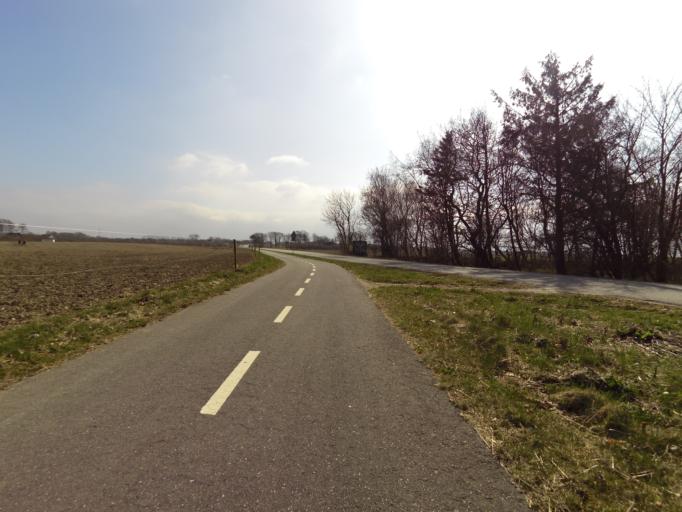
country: DK
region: Central Jutland
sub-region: Struer Kommune
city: Struer
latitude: 56.4490
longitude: 8.6223
